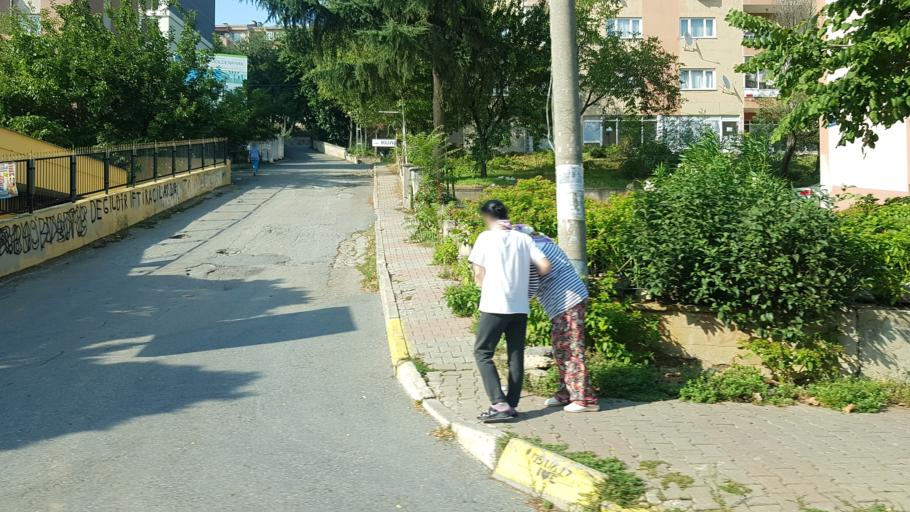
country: TR
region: Istanbul
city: Maltepe
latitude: 40.9222
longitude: 29.1652
